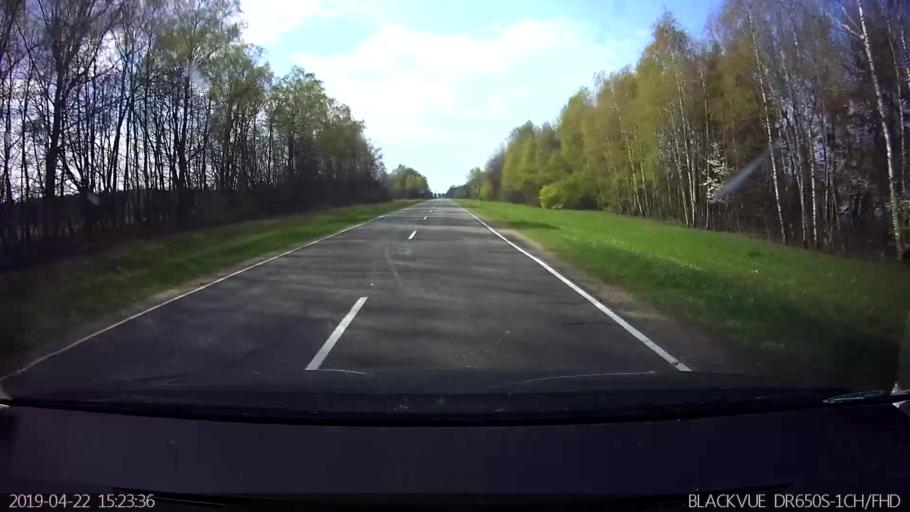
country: BY
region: Brest
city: Vysokaye
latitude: 52.3562
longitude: 23.4232
